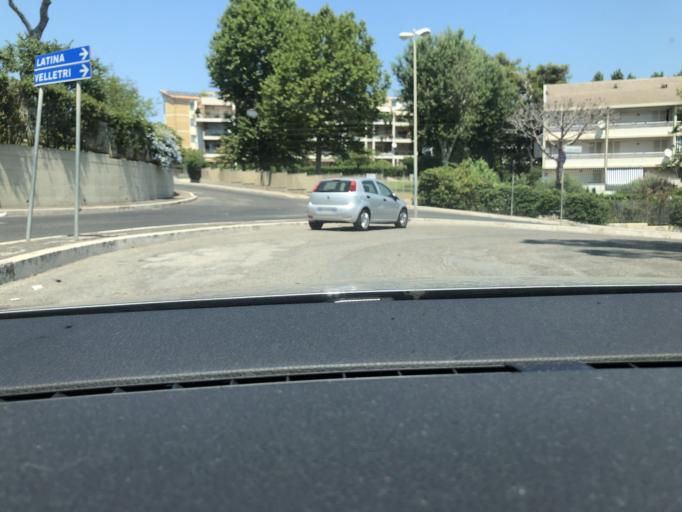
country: IT
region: Latium
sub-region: Citta metropolitana di Roma Capitale
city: Nettuno
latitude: 41.4576
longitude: 12.6492
